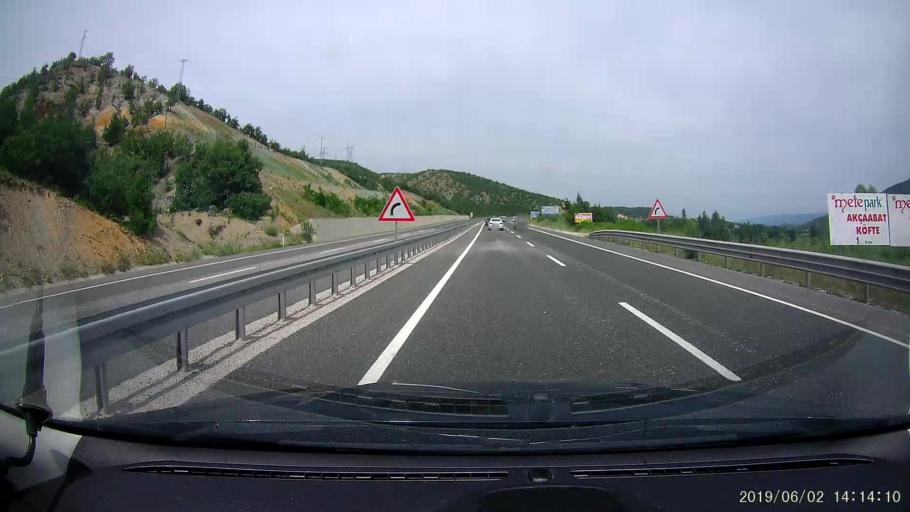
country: TR
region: Cankiri
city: Yaprakli
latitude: 40.9335
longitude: 33.8474
